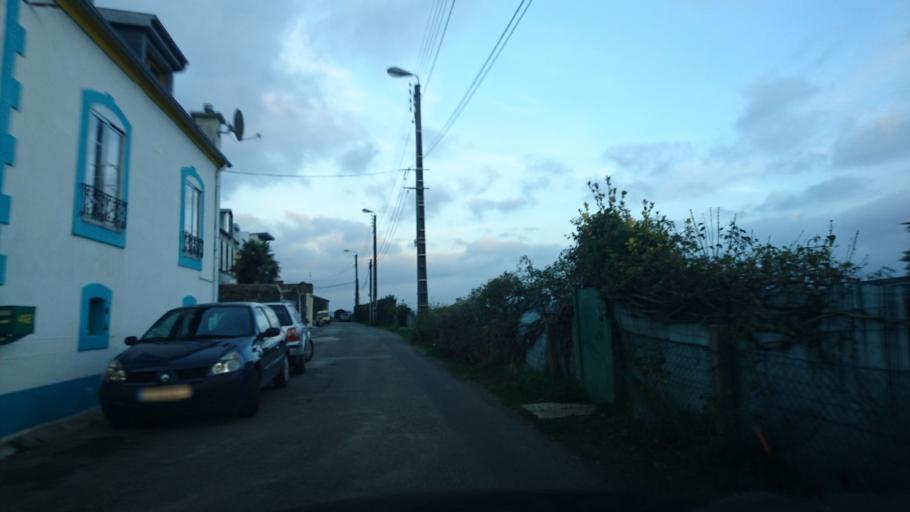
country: FR
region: Brittany
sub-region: Departement du Finistere
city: Brest
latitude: 48.3895
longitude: -4.4656
